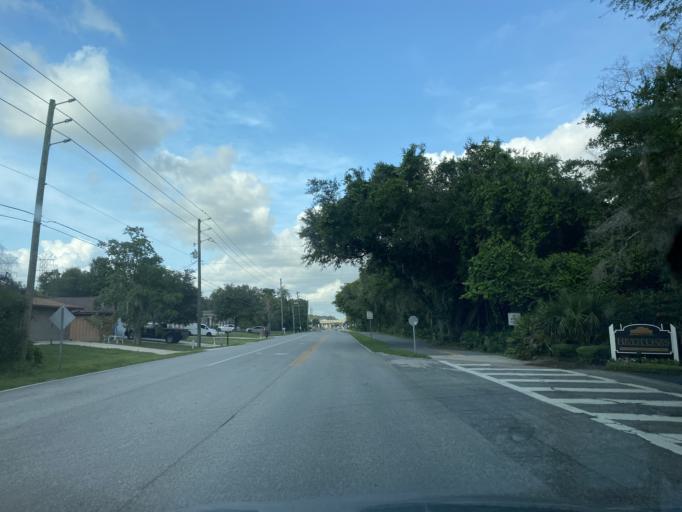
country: US
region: Florida
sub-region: Volusia County
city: DeBary
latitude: 28.8703
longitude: -81.2905
